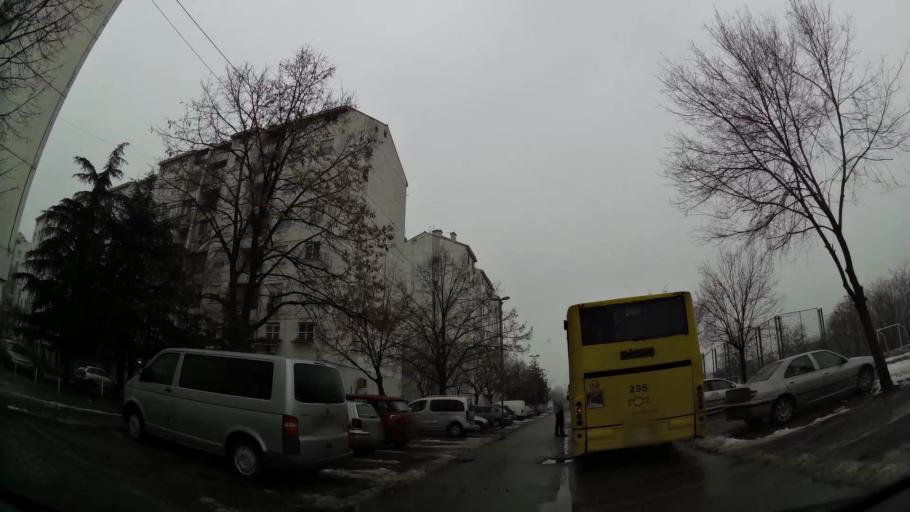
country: RS
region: Central Serbia
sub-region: Belgrade
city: Cukarica
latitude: 44.7782
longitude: 20.4051
